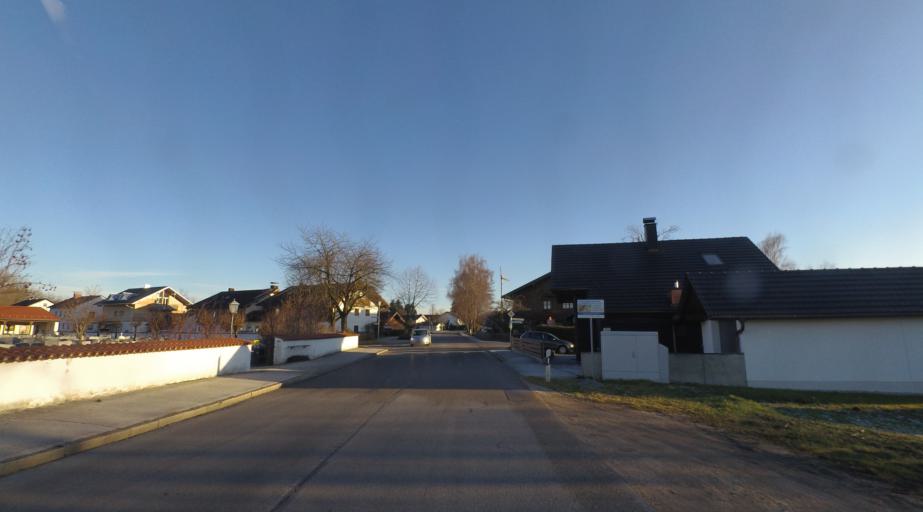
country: DE
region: Bavaria
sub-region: Upper Bavaria
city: Kirchanschoring
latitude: 47.9566
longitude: 12.8313
